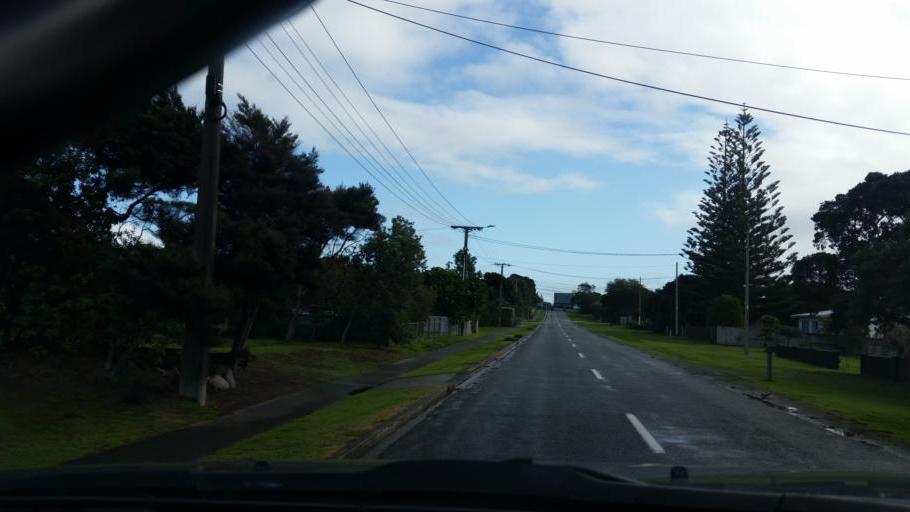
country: NZ
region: Auckland
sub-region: Auckland
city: Wellsford
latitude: -36.0906
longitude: 174.5878
